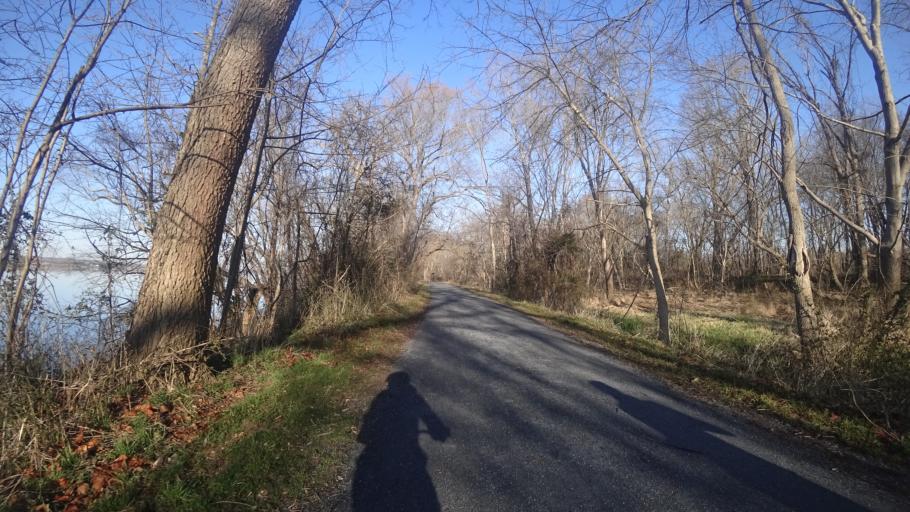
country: US
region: Virginia
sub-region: Loudoun County
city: Lowes Island
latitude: 39.0676
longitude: -77.3303
